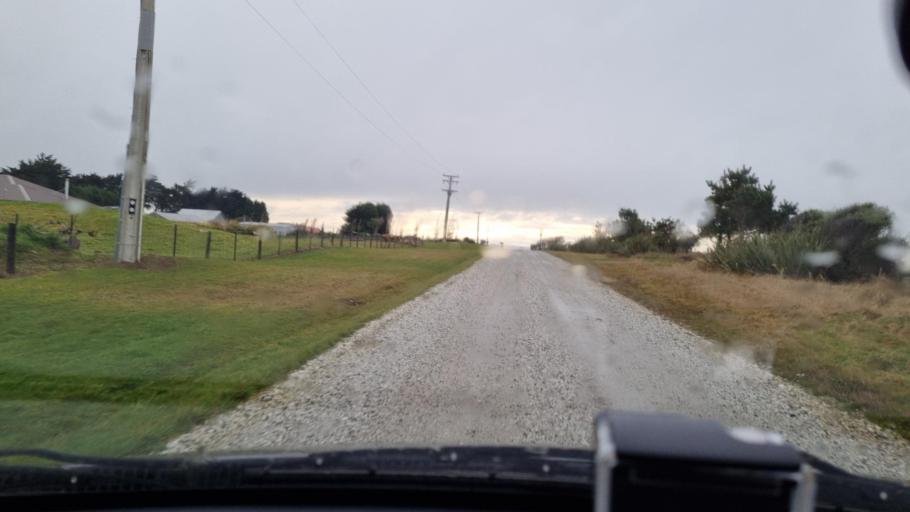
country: NZ
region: Southland
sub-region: Invercargill City
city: Invercargill
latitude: -46.4121
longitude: 168.2634
